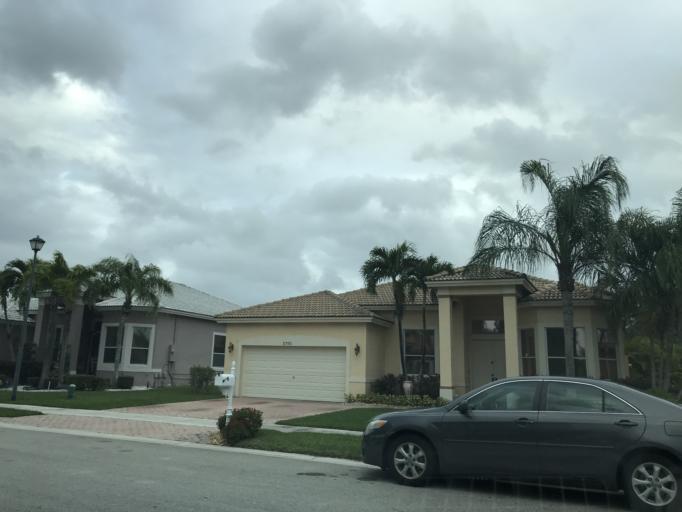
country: US
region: Florida
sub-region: Broward County
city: Coral Springs
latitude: 26.3003
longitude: -80.2748
